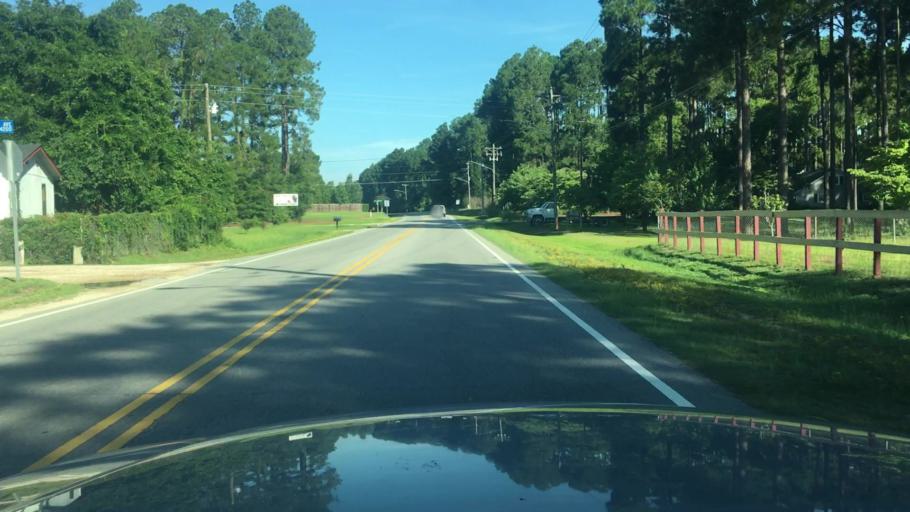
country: US
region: North Carolina
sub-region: Cumberland County
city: Fayetteville
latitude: 35.1278
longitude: -78.8923
